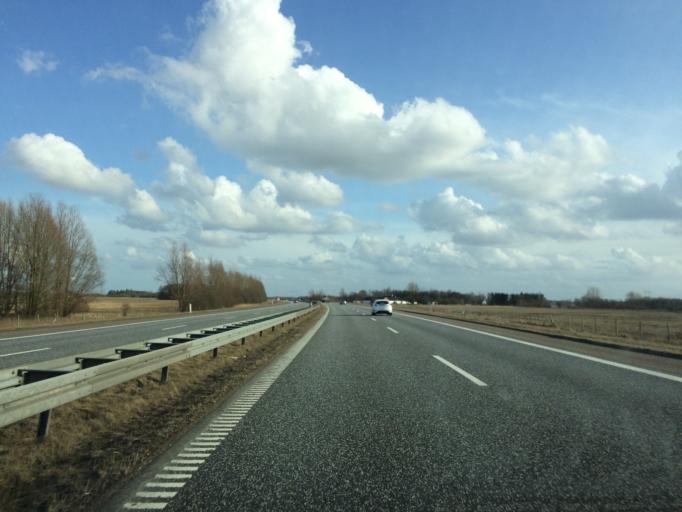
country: DK
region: North Denmark
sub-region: Alborg Kommune
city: Vestbjerg
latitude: 57.1194
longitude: 9.9433
